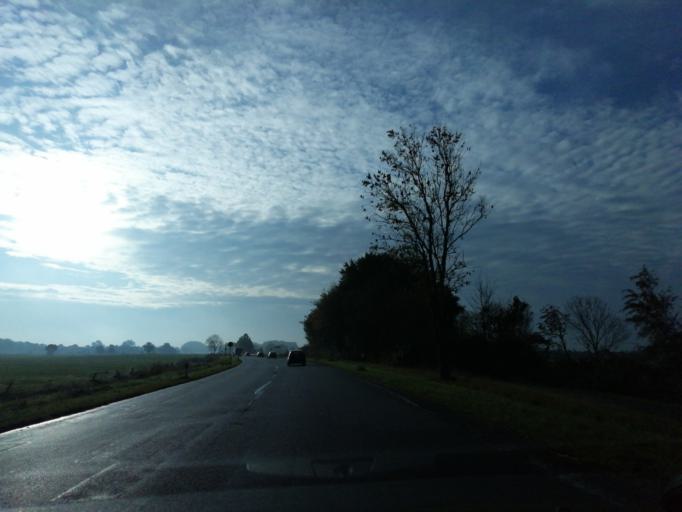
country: DE
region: Lower Saxony
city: Fedderwarden
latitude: 53.6046
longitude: 8.0459
